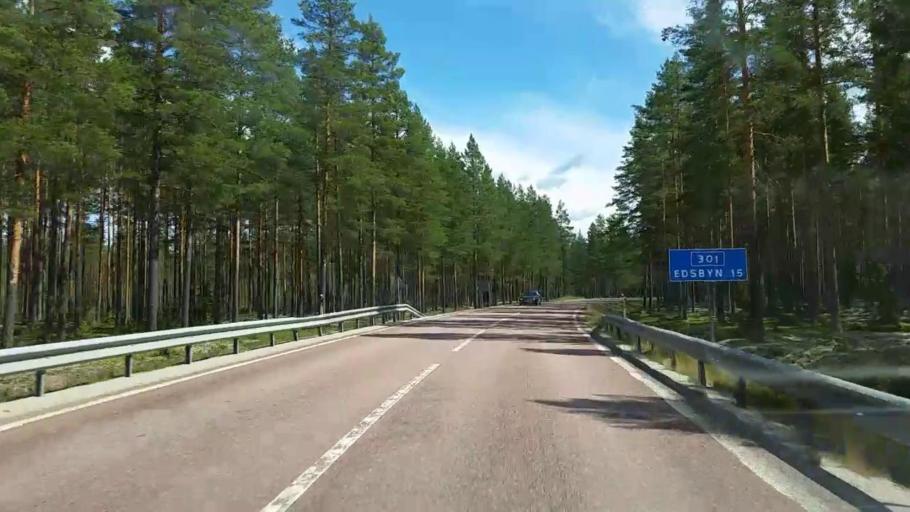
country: SE
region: Gaevleborg
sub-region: Ovanakers Kommun
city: Edsbyn
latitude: 61.3516
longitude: 15.5850
